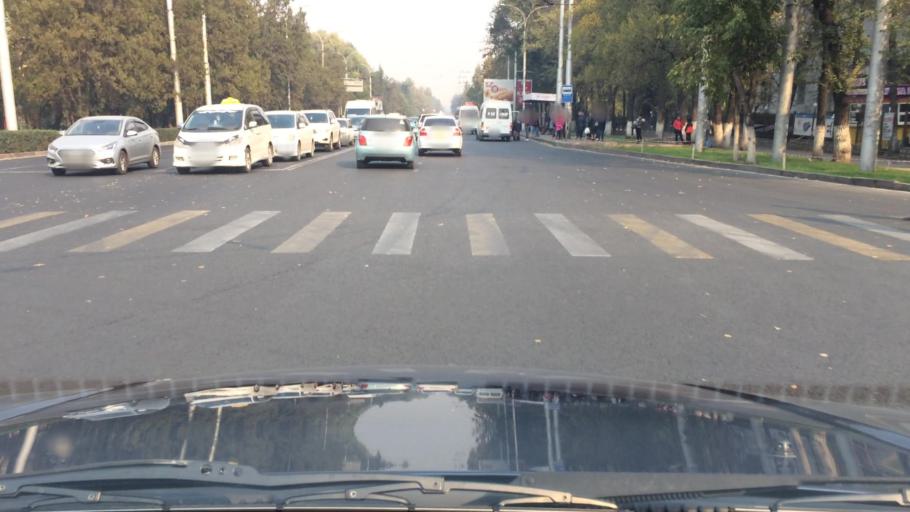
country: KG
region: Chuy
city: Bishkek
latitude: 42.8437
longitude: 74.5861
